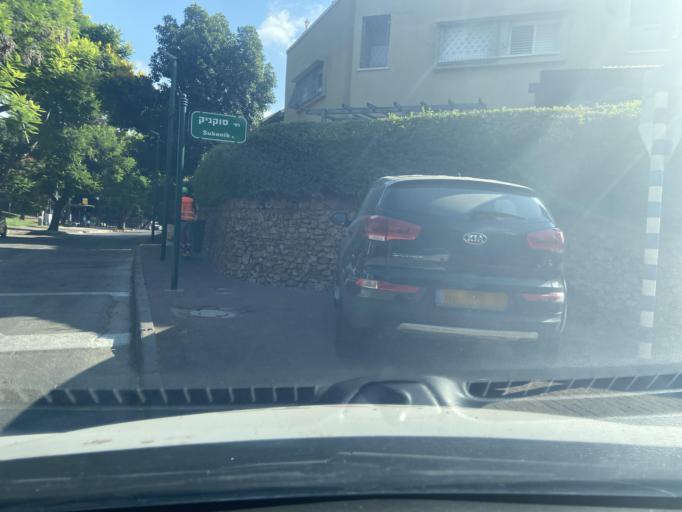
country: IL
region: Central District
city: Yehud
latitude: 32.0369
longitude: 34.8938
